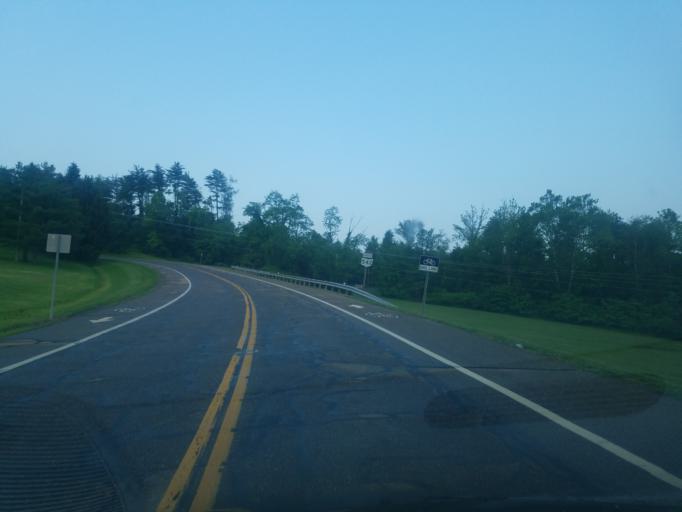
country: US
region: Ohio
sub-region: Tuscarawas County
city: Rockford
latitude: 40.5462
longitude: -81.2447
